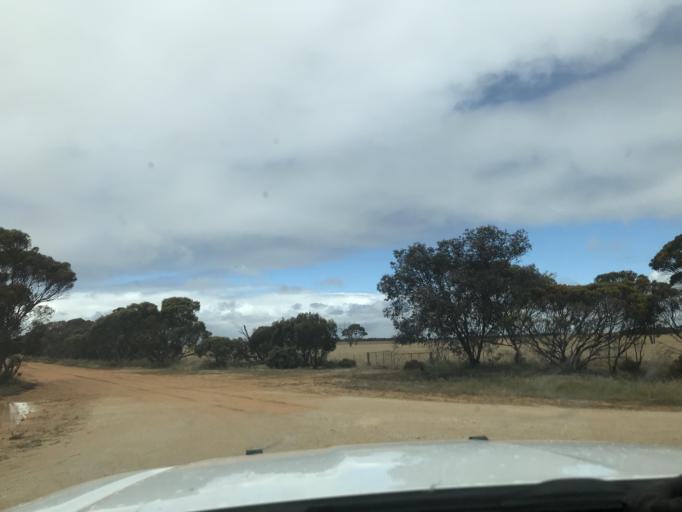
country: AU
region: South Australia
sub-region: Tatiara
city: Bordertown
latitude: -36.1457
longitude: 141.2335
